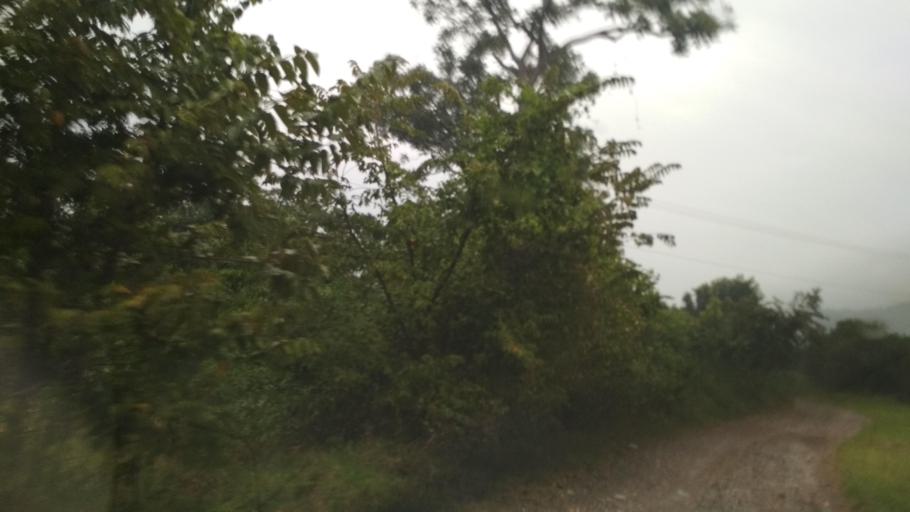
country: MM
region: Shan
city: Taunggyi
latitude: 20.3052
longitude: 97.3014
